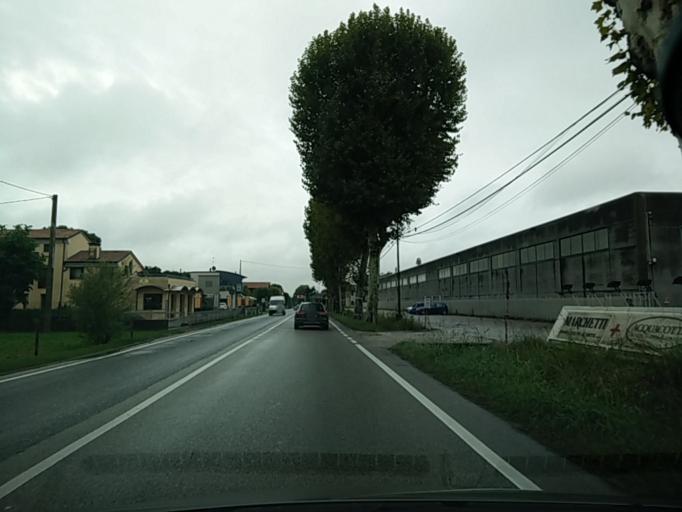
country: IT
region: Veneto
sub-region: Provincia di Vicenza
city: Belvedere
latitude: 45.6707
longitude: 11.7770
